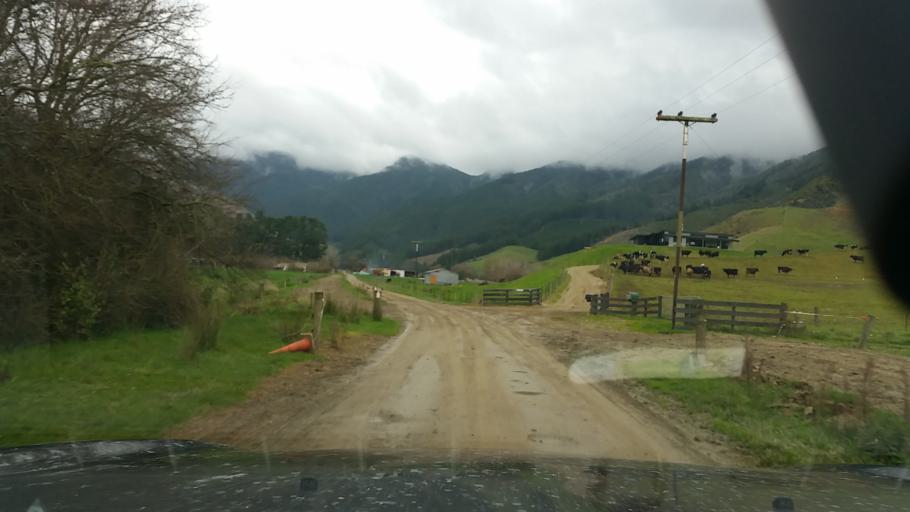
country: NZ
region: Marlborough
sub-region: Marlborough District
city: Picton
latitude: -41.2990
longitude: 173.8550
